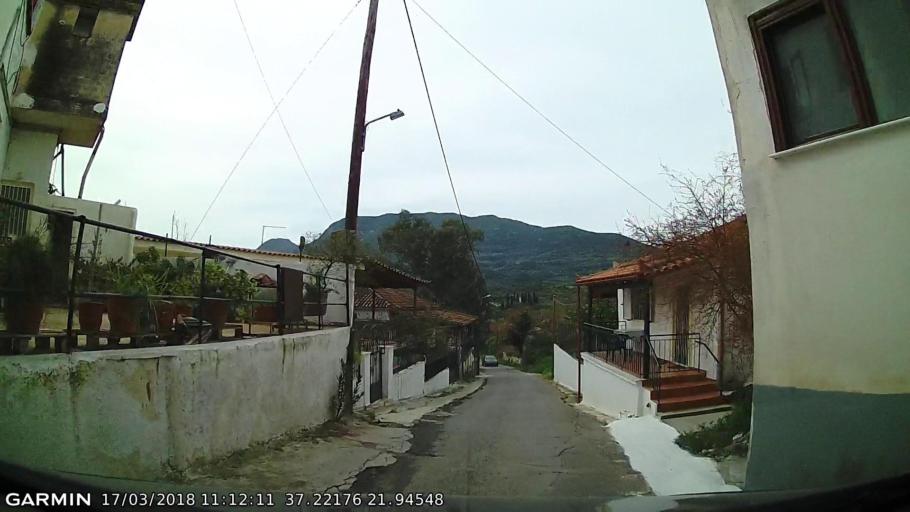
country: GR
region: Peloponnese
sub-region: Nomos Messinias
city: Meligalas
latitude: 37.2217
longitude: 21.9454
